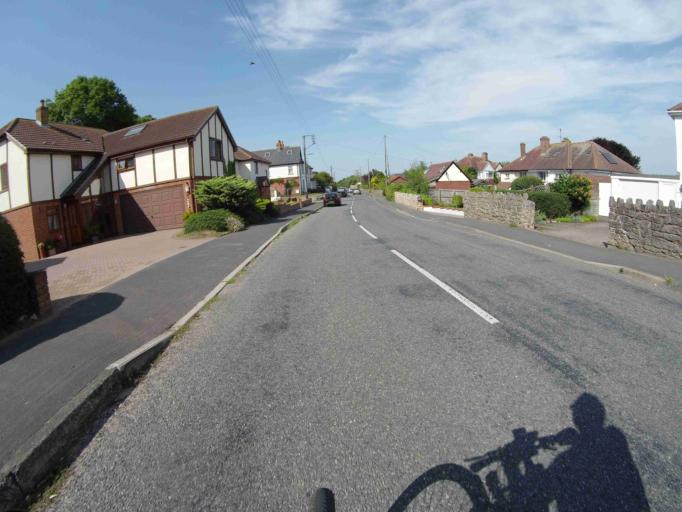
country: GB
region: England
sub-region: Devon
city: Budleigh Salterton
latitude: 50.6363
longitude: -3.3188
